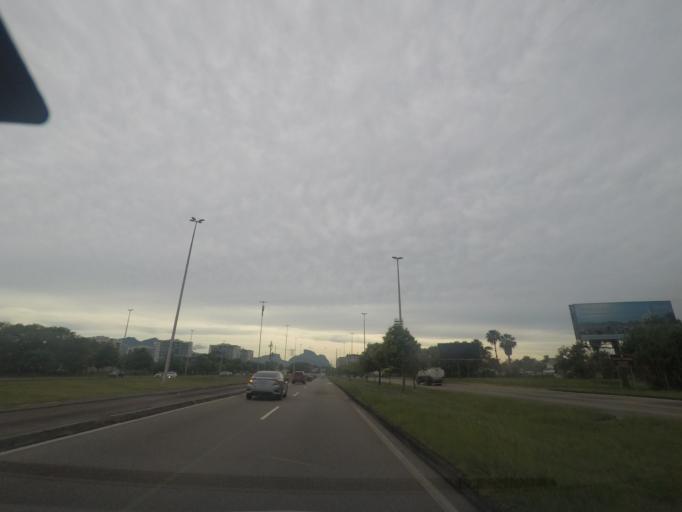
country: BR
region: Rio de Janeiro
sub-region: Nilopolis
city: Nilopolis
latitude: -23.0002
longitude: -43.4026
